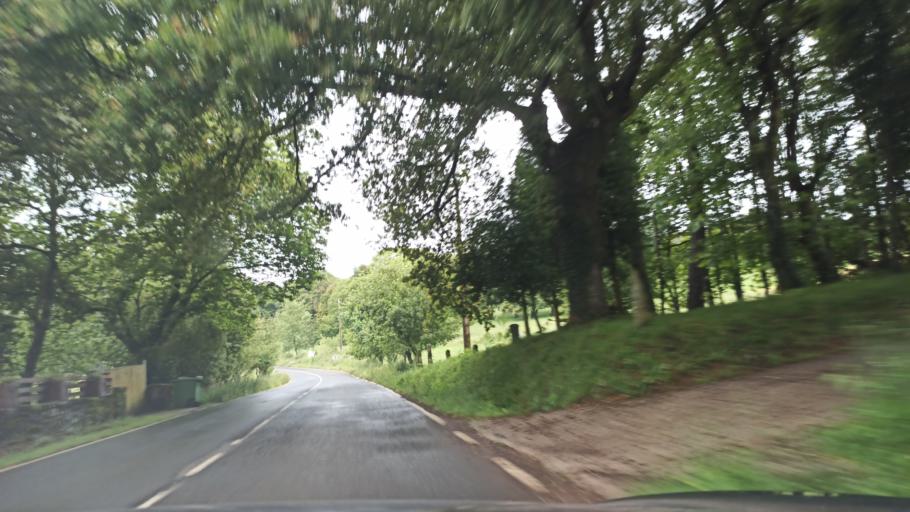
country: ES
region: Galicia
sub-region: Provincia da Coruna
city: Santiso
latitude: 42.7853
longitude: -8.0588
